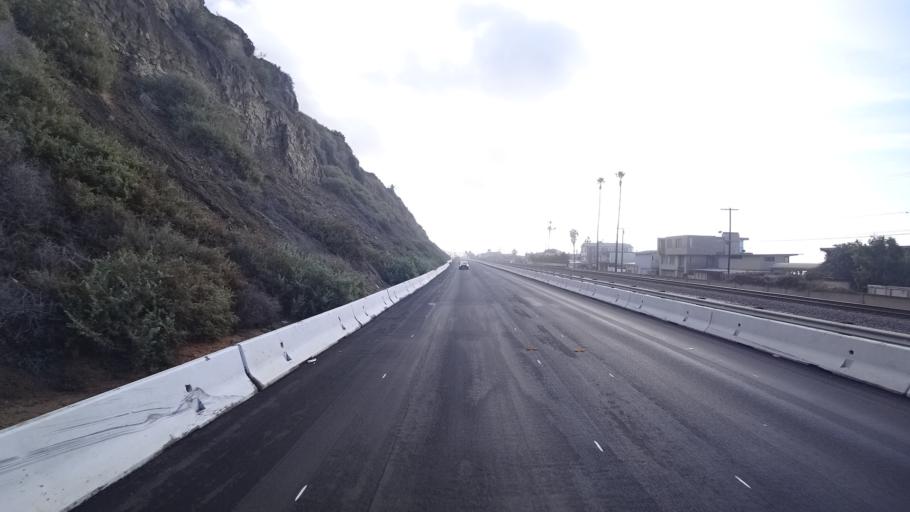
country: US
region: California
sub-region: Orange County
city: San Clemente
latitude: 33.4440
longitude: -117.6490
